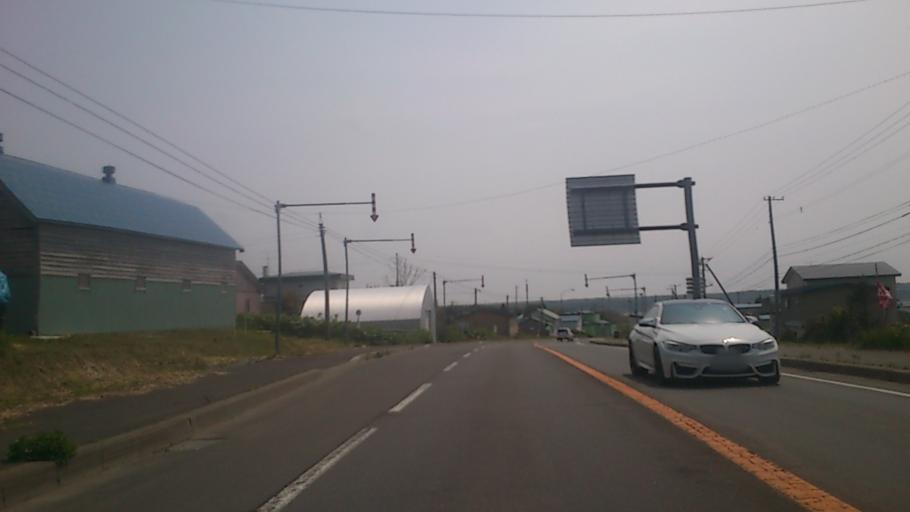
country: JP
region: Hokkaido
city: Nemuro
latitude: 43.2799
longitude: 145.5063
